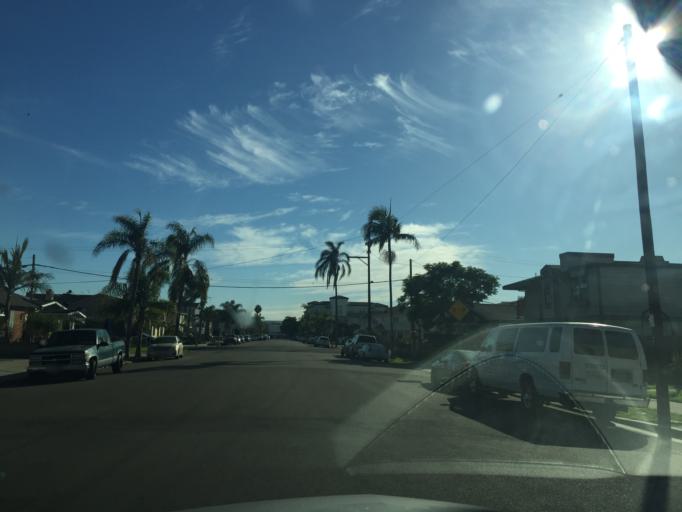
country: US
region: California
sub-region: San Diego County
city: San Diego
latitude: 32.7529
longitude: -117.1290
